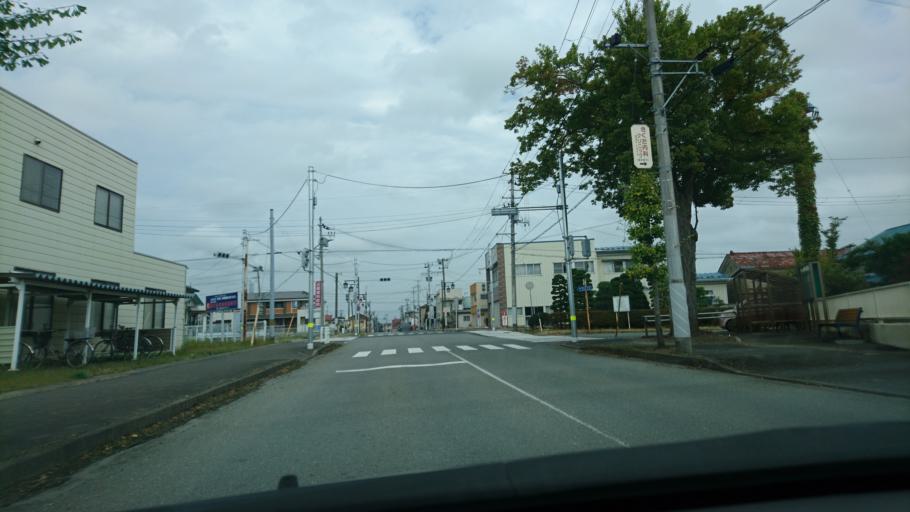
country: JP
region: Miyagi
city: Furukawa
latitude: 38.7313
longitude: 141.0262
